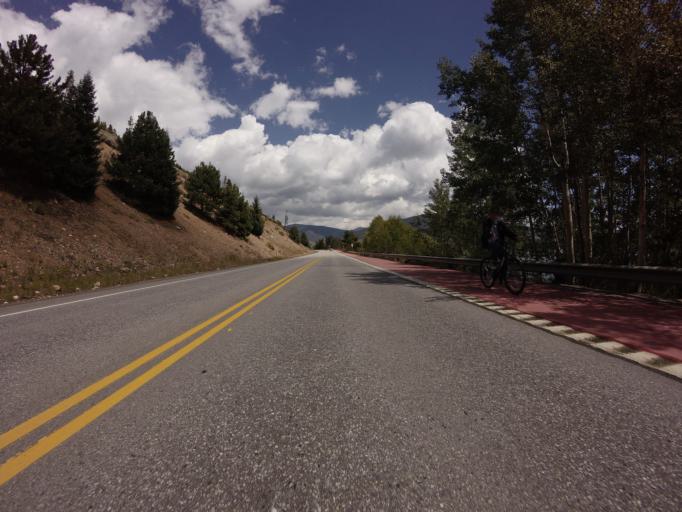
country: US
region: Colorado
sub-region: Summit County
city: Silverthorne
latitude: 39.6113
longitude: -106.0669
